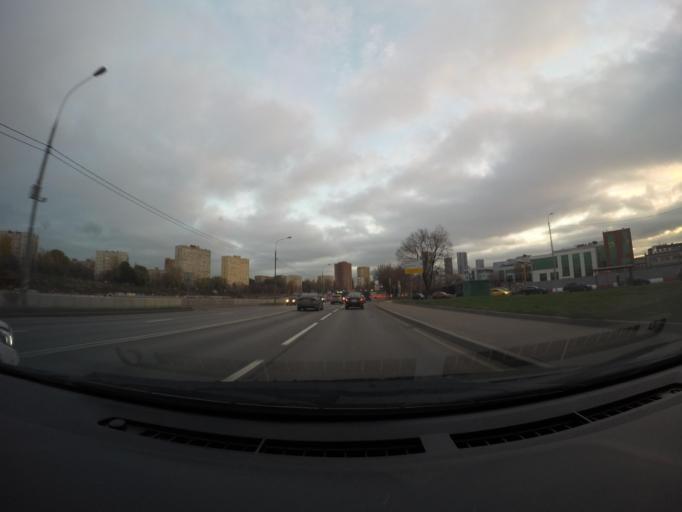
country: RU
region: Moscow
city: Taganskiy
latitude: 55.7259
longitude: 37.6555
